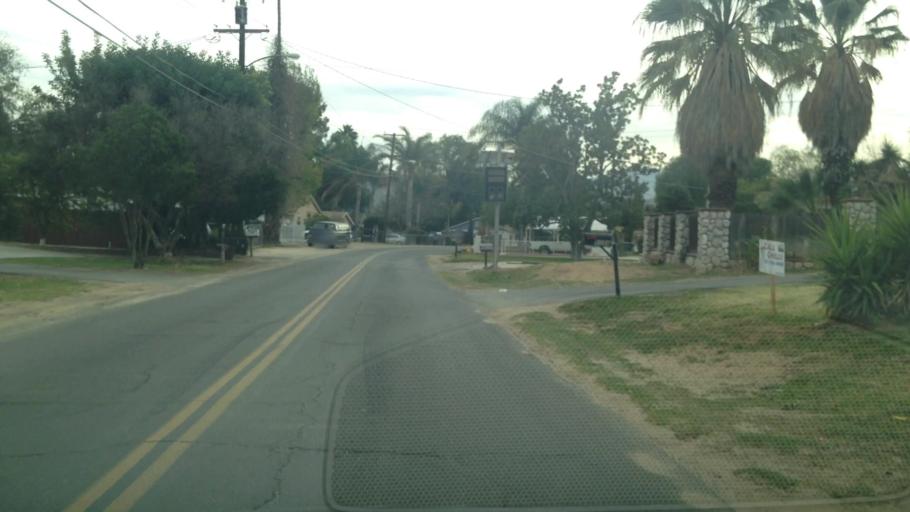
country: US
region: California
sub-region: Riverside County
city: Pedley
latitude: 33.9276
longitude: -117.4801
